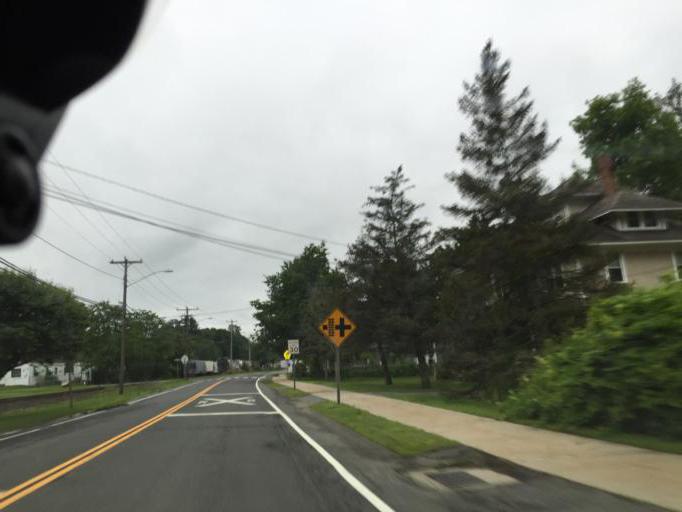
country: US
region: Connecticut
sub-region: Litchfield County
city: Canaan
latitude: 42.0314
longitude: -73.3277
